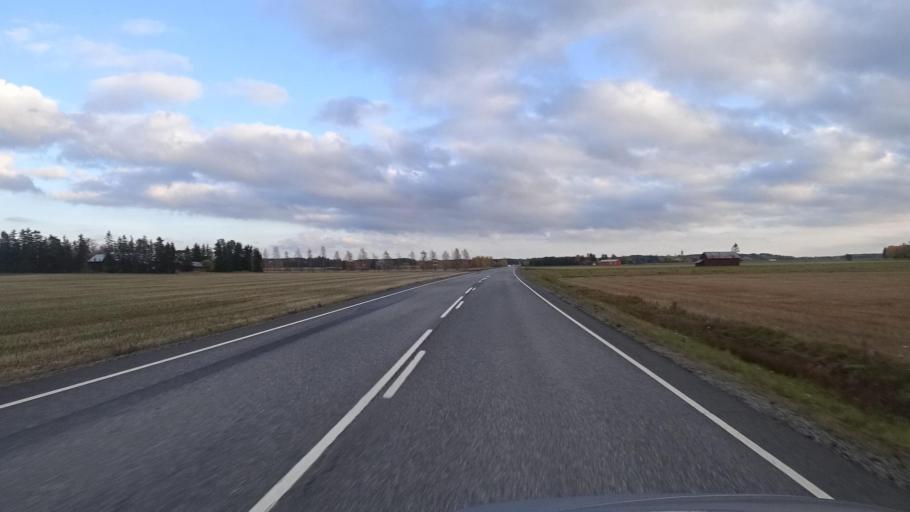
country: FI
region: Varsinais-Suomi
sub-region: Loimaa
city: Alastaro
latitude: 60.8971
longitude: 22.9562
